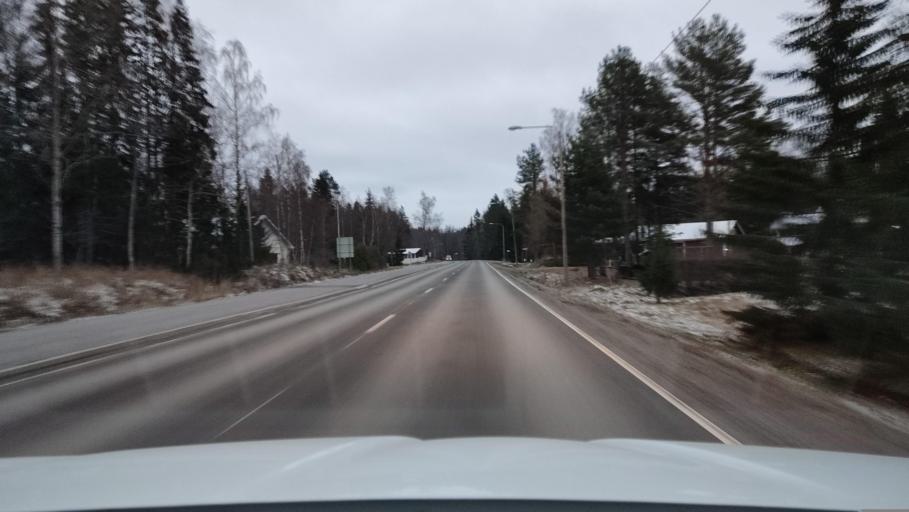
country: FI
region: Ostrobothnia
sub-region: Vaasa
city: Replot
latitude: 63.2197
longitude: 21.4183
